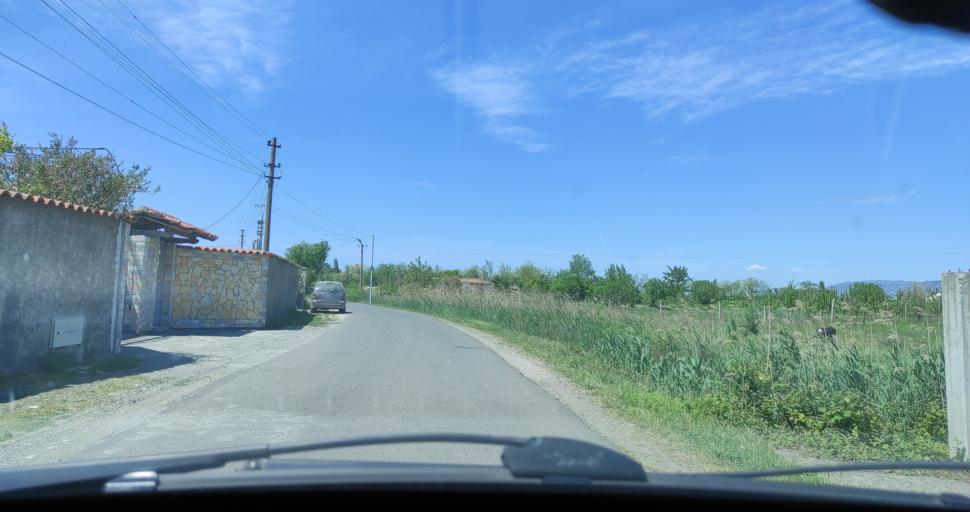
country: AL
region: Lezhe
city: Lezhe
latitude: 41.7565
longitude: 19.6141
